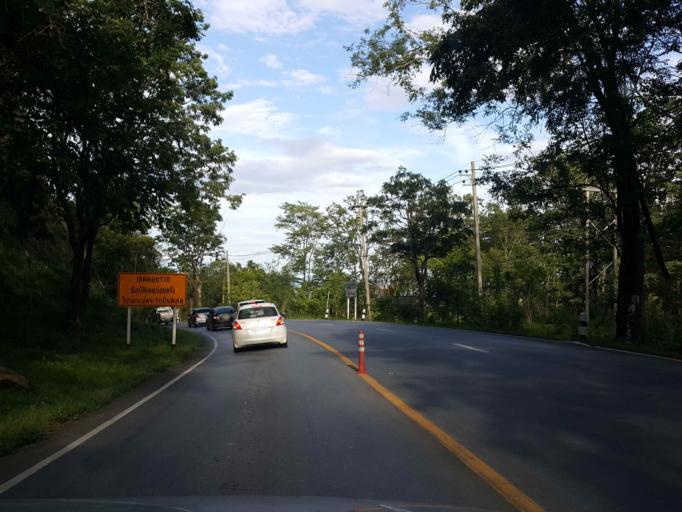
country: TH
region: Tak
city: Tak
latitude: 16.8134
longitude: 98.9662
